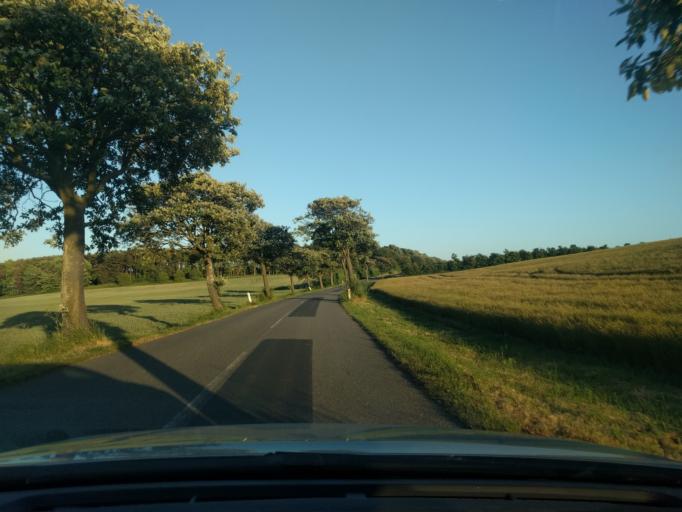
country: DK
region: South Denmark
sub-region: Kerteminde Kommune
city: Kerteminde
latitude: 55.5794
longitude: 10.6421
